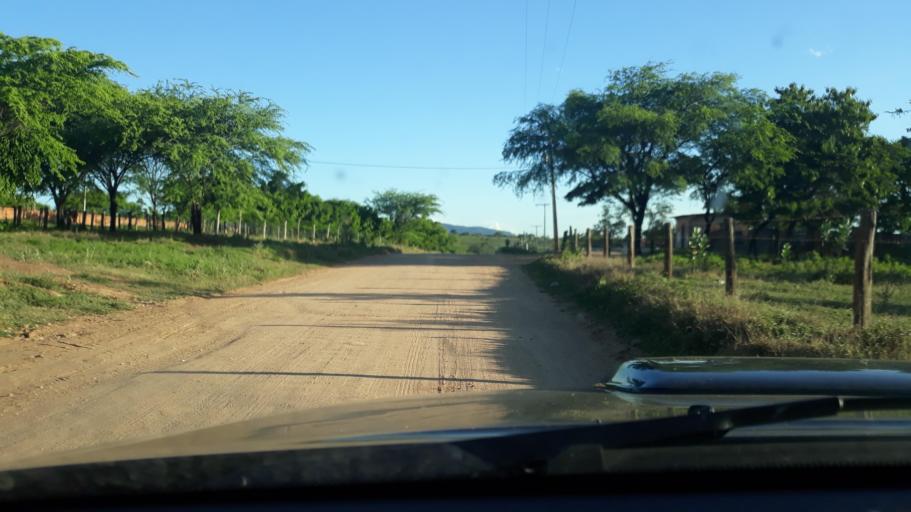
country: BR
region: Bahia
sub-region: Riacho De Santana
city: Riacho de Santana
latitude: -13.7860
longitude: -42.7133
